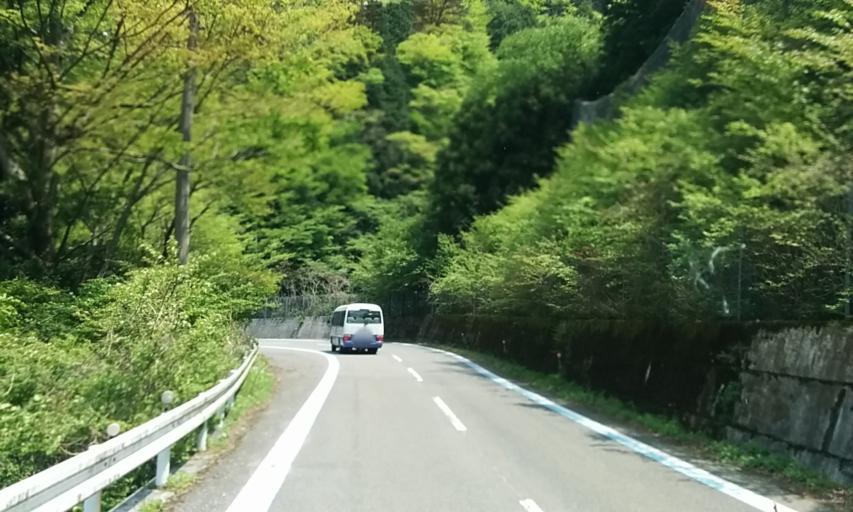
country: JP
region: Ehime
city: Niihama
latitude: 33.8721
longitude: 133.2943
